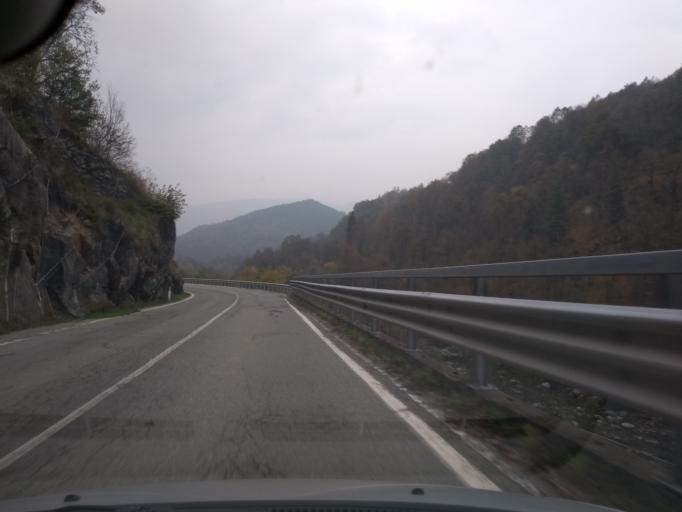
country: IT
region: Piedmont
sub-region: Provincia di Torino
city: Traves
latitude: 45.2739
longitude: 7.4296
